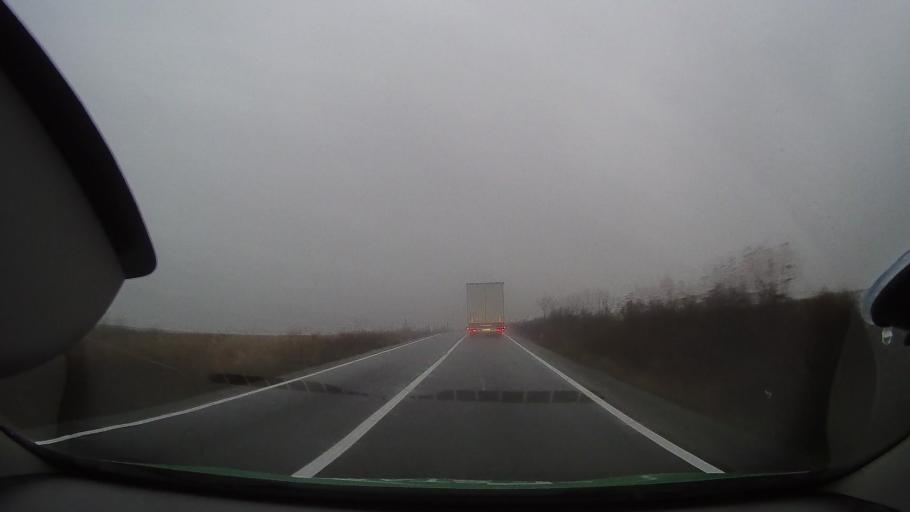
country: RO
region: Bihor
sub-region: Comuna Olcea
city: Calacea
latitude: 46.6534
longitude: 21.9595
